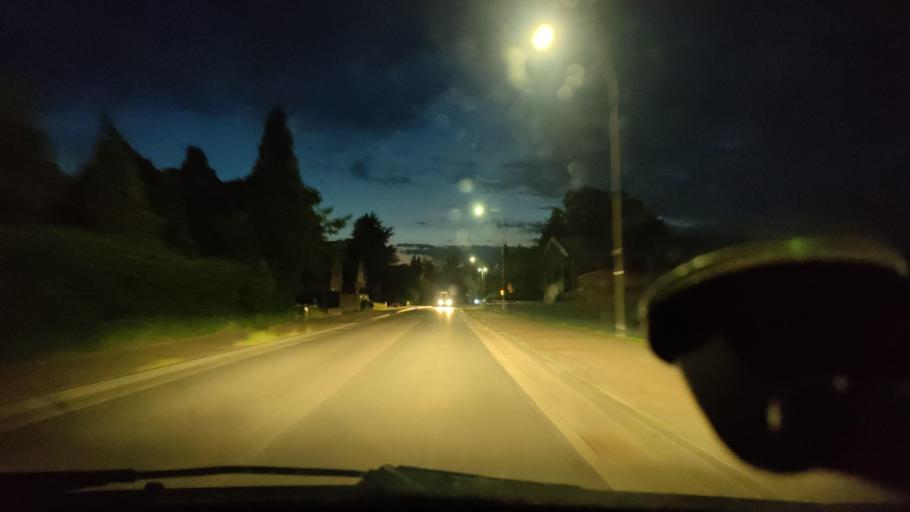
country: DE
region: North Rhine-Westphalia
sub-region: Regierungsbezirk Dusseldorf
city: Alpen
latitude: 51.5896
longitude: 6.5616
